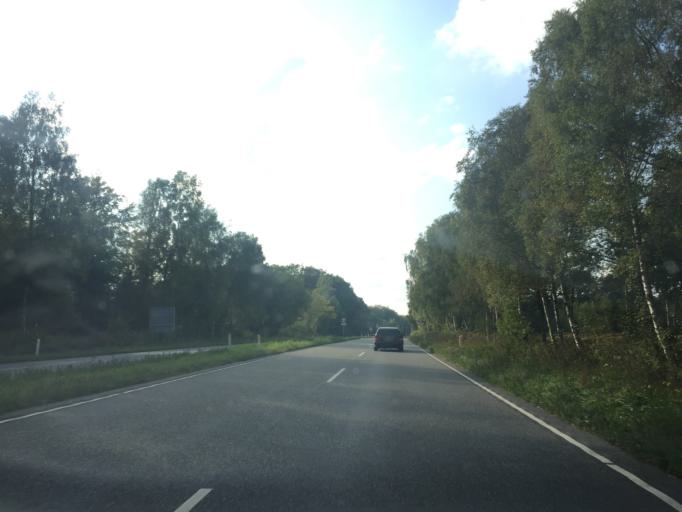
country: DK
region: Zealand
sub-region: Holbaek Kommune
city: Jyderup
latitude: 55.6638
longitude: 11.4008
